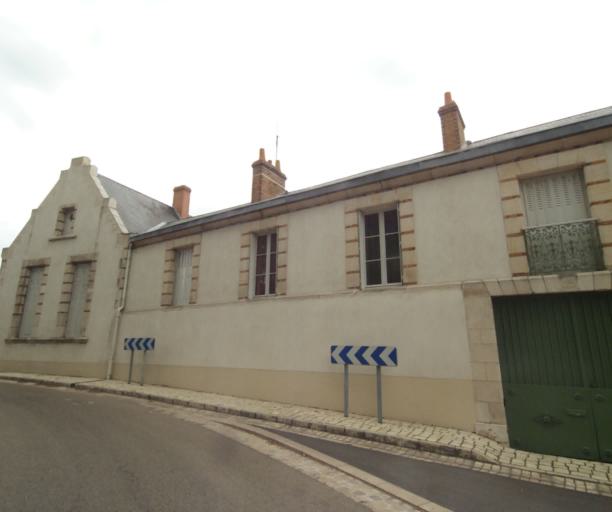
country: FR
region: Centre
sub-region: Departement du Loiret
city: Saint-Hilaire-Saint-Mesmin
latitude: 47.8733
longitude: 1.8401
